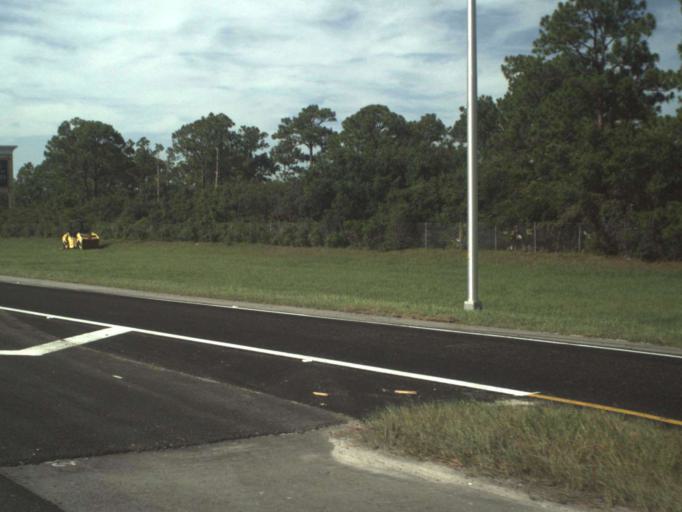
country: US
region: Florida
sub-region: Indian River County
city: West Vero Corridor
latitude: 27.6352
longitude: -80.5165
